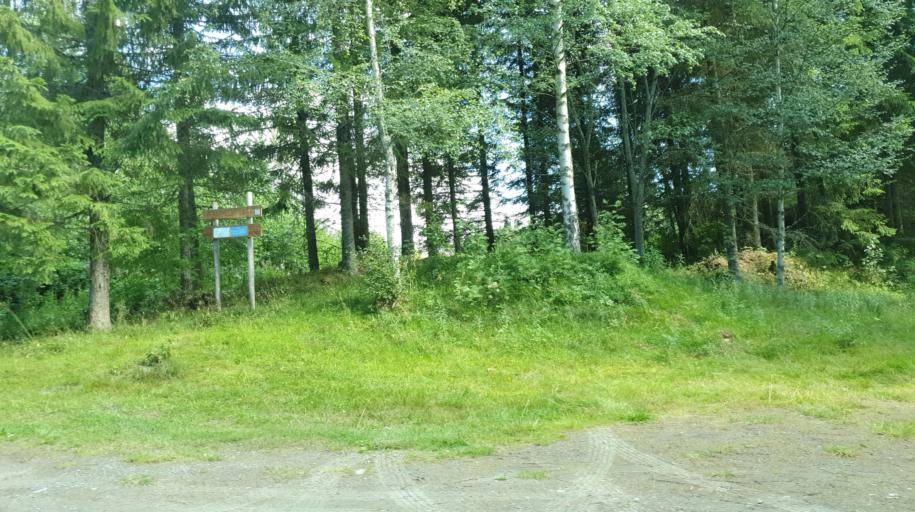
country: NO
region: Nord-Trondelag
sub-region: Levanger
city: Levanger
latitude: 63.6960
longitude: 11.2773
